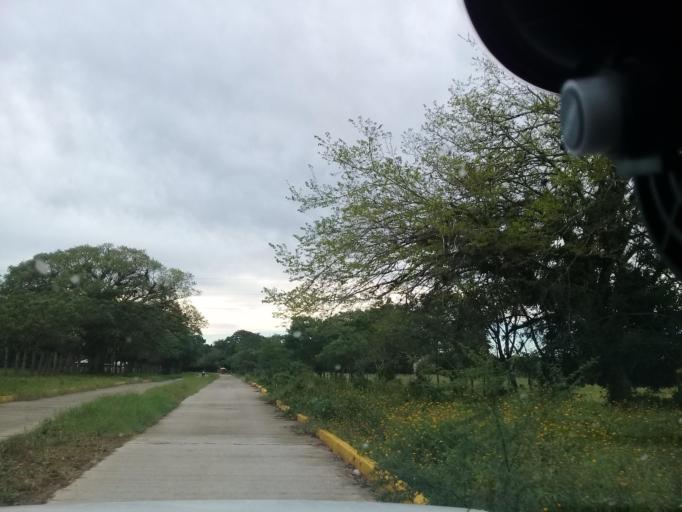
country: MX
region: Hidalgo
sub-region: Huejutla de Reyes
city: Chalahuiyapa
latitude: 21.1623
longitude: -98.3605
